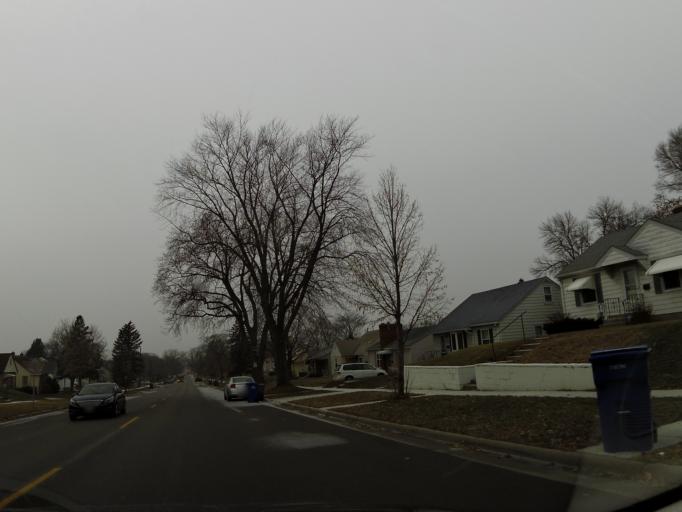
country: US
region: Minnesota
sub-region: Ramsey County
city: Maplewood
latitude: 44.9568
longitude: -93.0281
